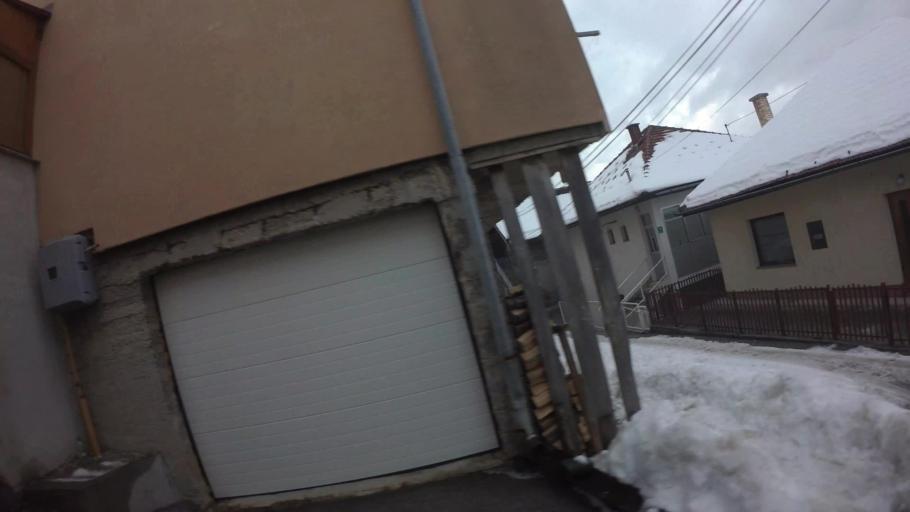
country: BA
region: Federation of Bosnia and Herzegovina
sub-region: Kanton Sarajevo
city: Sarajevo
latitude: 43.8563
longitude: 18.3486
